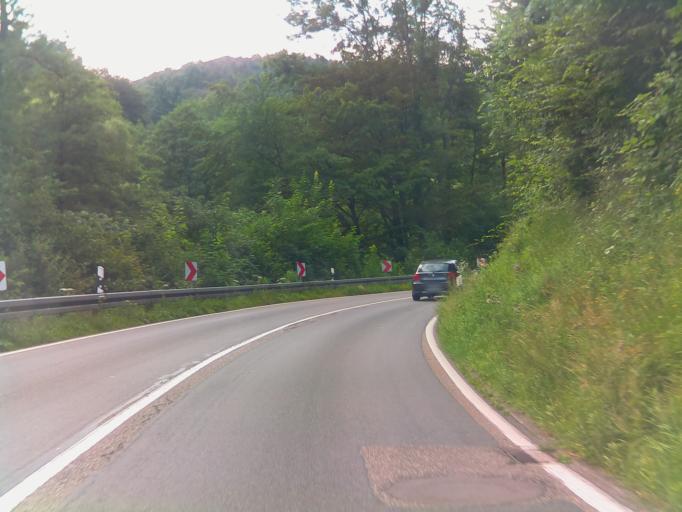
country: DE
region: Baden-Wuerttemberg
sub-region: Karlsruhe Region
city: Schonau
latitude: 49.4150
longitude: 8.8083
